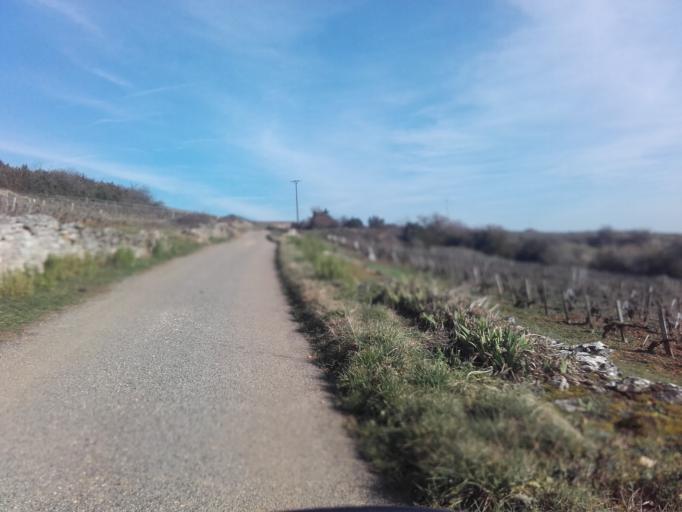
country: FR
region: Bourgogne
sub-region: Departement de Saone-et-Loire
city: Chagny
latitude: 46.9181
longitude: 4.7053
